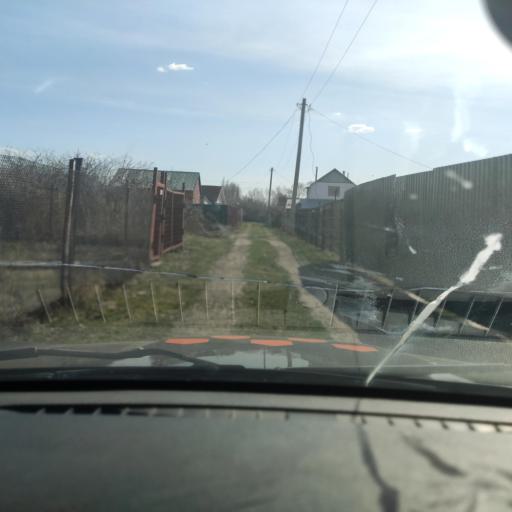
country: RU
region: Samara
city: Tol'yatti
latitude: 53.7035
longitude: 49.4118
